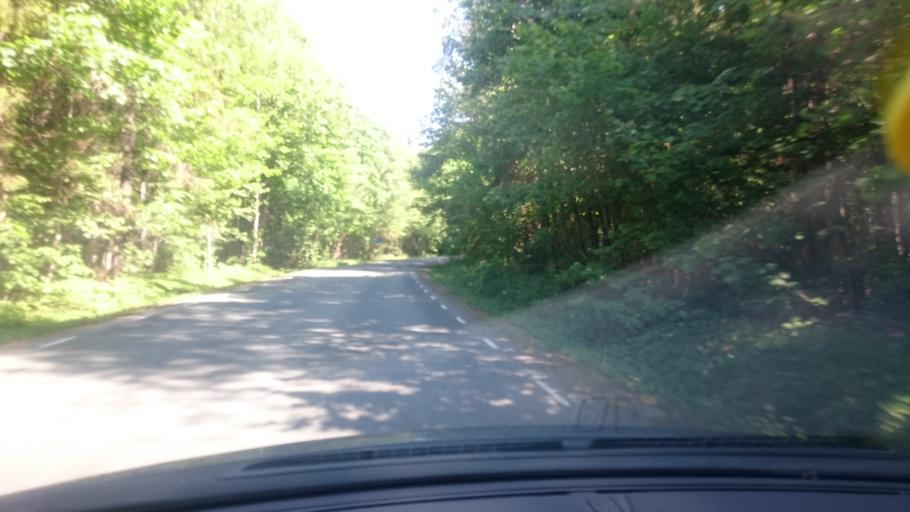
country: EE
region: Harju
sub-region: Rae vald
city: Vaida
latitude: 59.2062
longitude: 24.9322
